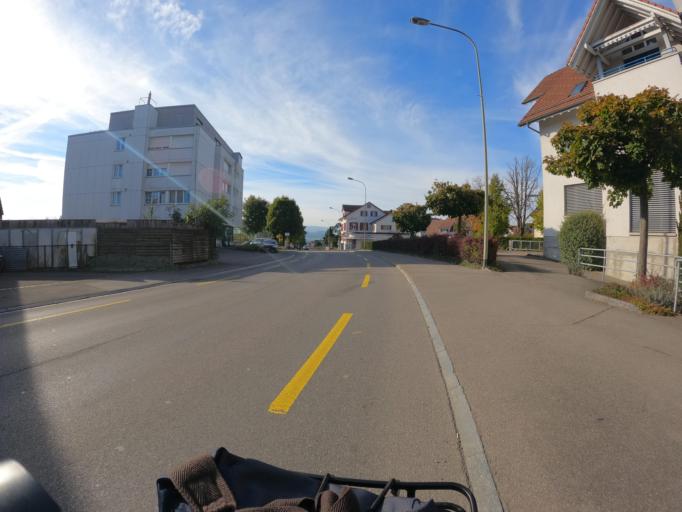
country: CH
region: Zurich
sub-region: Bezirk Affoltern
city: Obfelden / Oberlunnern
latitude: 47.2619
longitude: 8.4171
